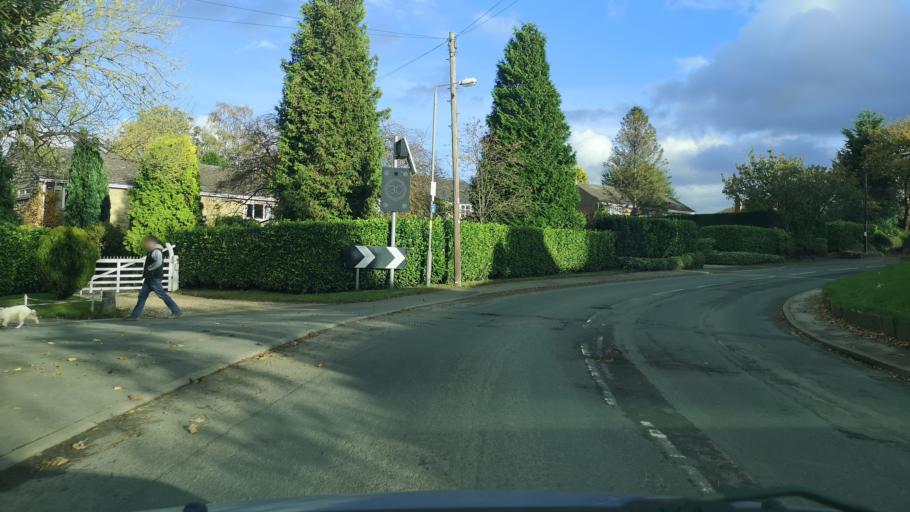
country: GB
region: England
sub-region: City and Borough of Wakefield
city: Notton
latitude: 53.6140
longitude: -1.4766
